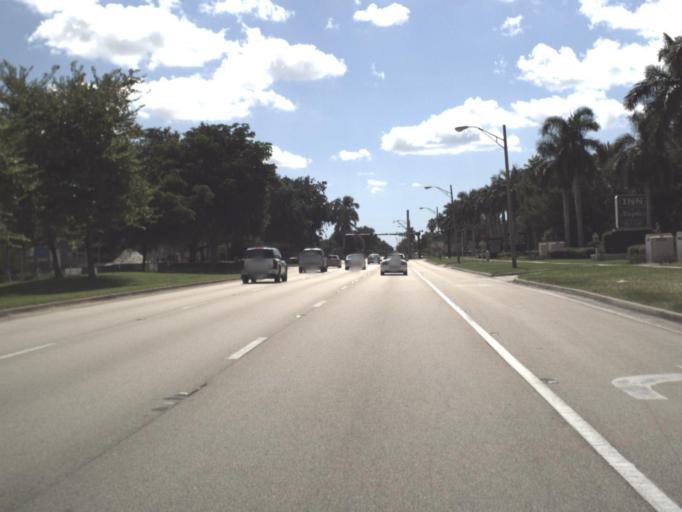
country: US
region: Florida
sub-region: Collier County
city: Pine Ridge
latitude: 26.1948
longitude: -81.8002
